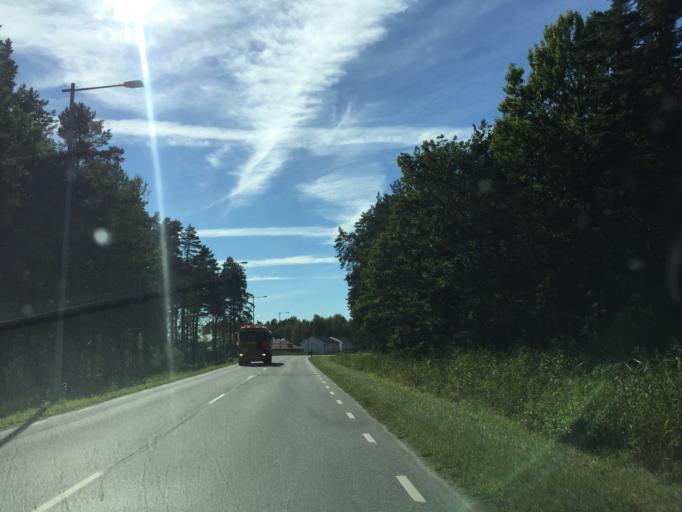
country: SE
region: OErebro
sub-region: Orebro Kommun
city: Orebro
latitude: 59.2893
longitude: 15.2448
